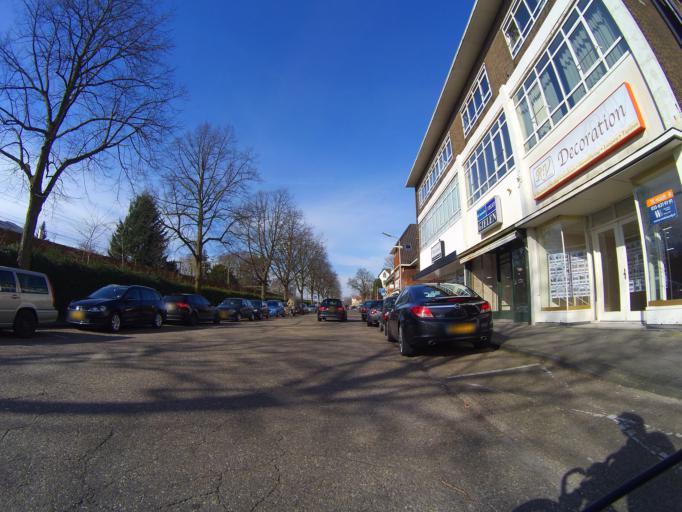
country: NL
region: North Holland
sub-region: Gemeente Bussum
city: Bussum
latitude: 52.2766
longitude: 5.1591
